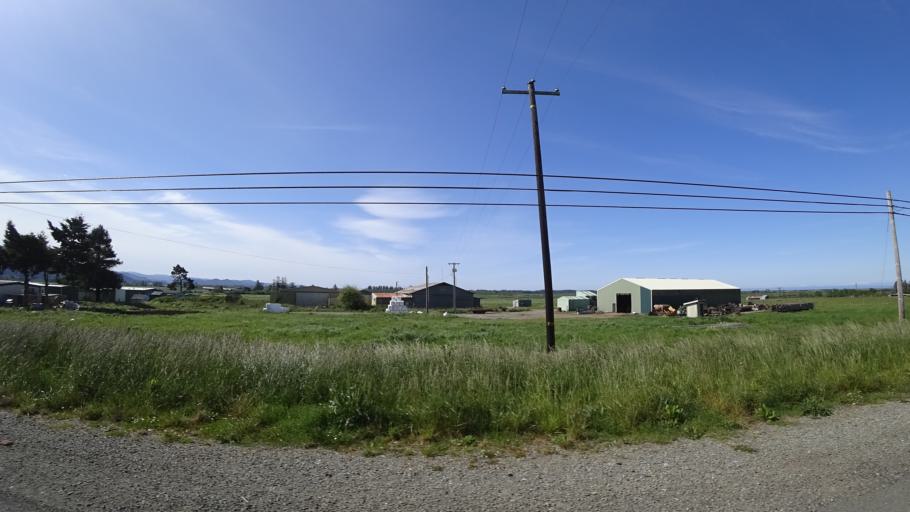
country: US
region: Oregon
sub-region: Curry County
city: Harbor
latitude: 41.9346
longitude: -124.1692
